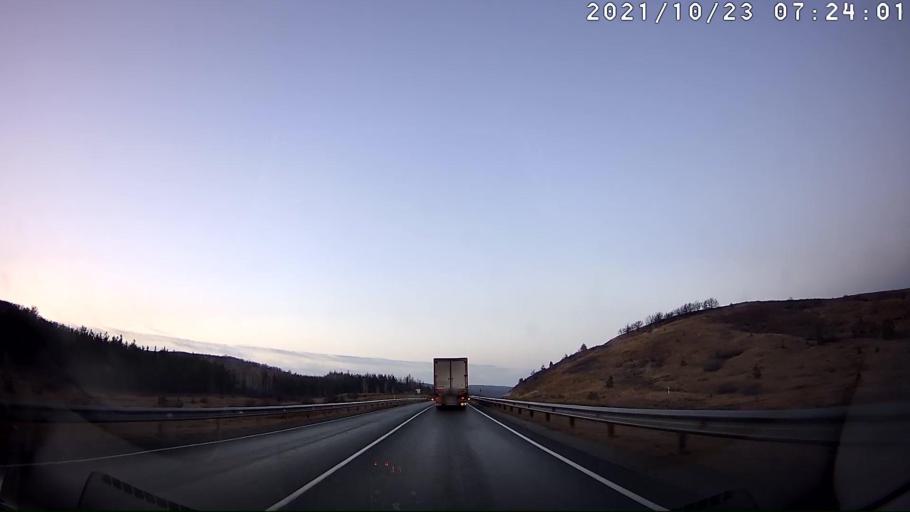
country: RU
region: Saratov
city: Alekseyevka
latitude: 52.3756
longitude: 47.9711
